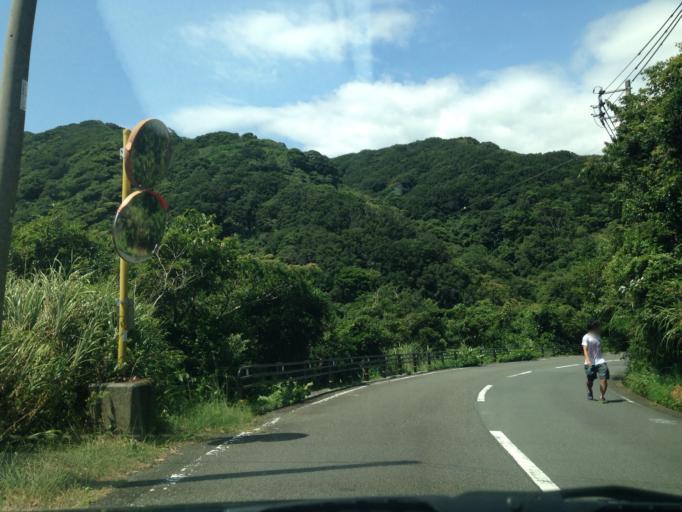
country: JP
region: Shizuoka
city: Shimoda
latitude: 34.6192
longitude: 138.8231
